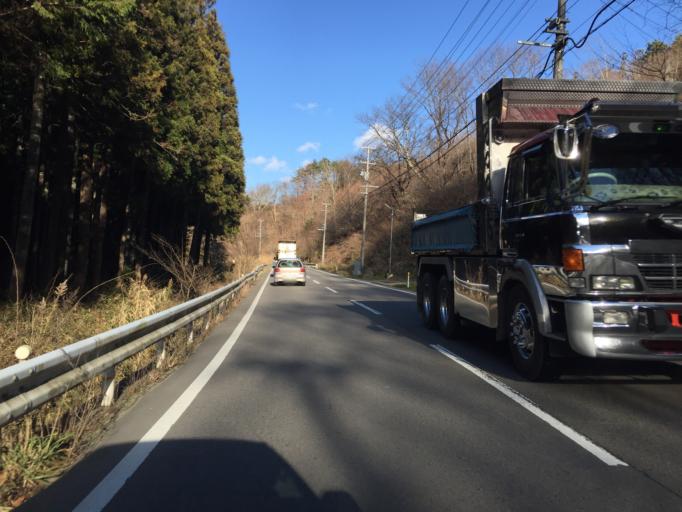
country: JP
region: Fukushima
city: Ishikawa
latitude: 37.2404
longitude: 140.6312
